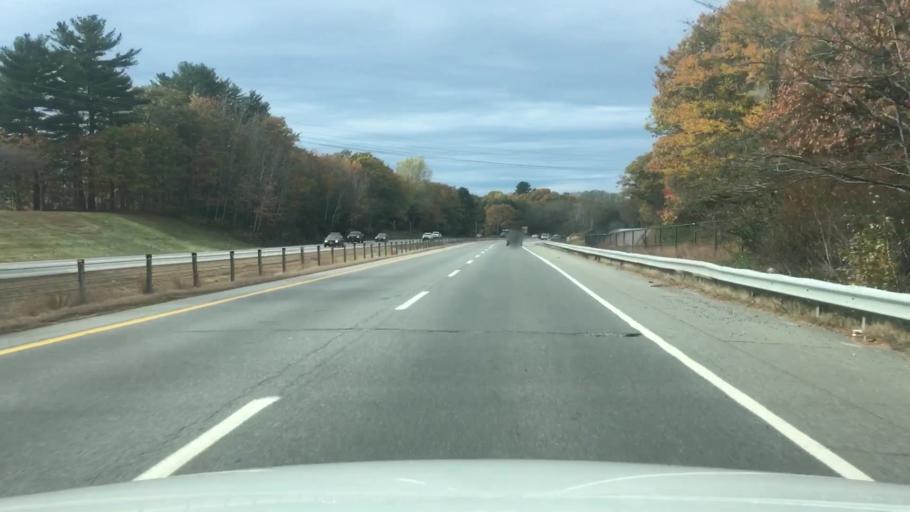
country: US
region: Maine
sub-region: Cumberland County
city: Brunswick
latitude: 43.9094
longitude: -69.9224
